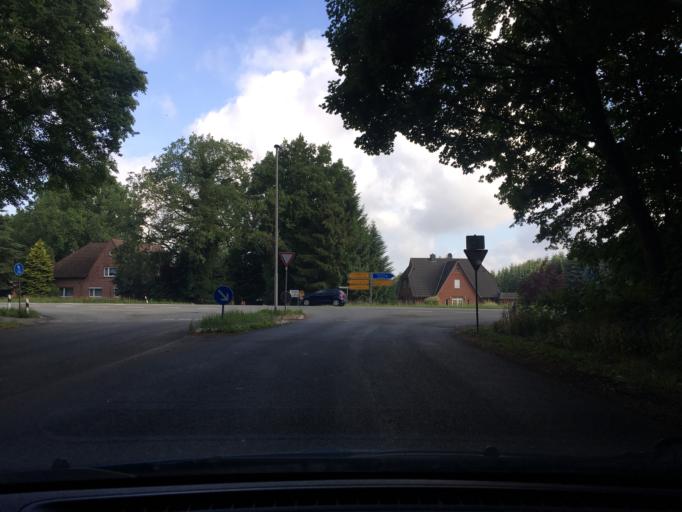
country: DE
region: Lower Saxony
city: Buchholz in der Nordheide
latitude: 53.3306
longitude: 9.8320
